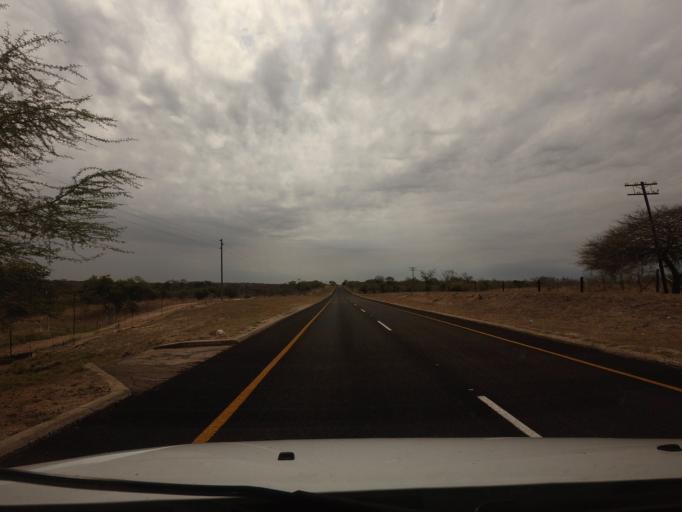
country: ZA
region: Limpopo
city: Thulamahashi
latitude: -24.5608
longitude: 31.1625
